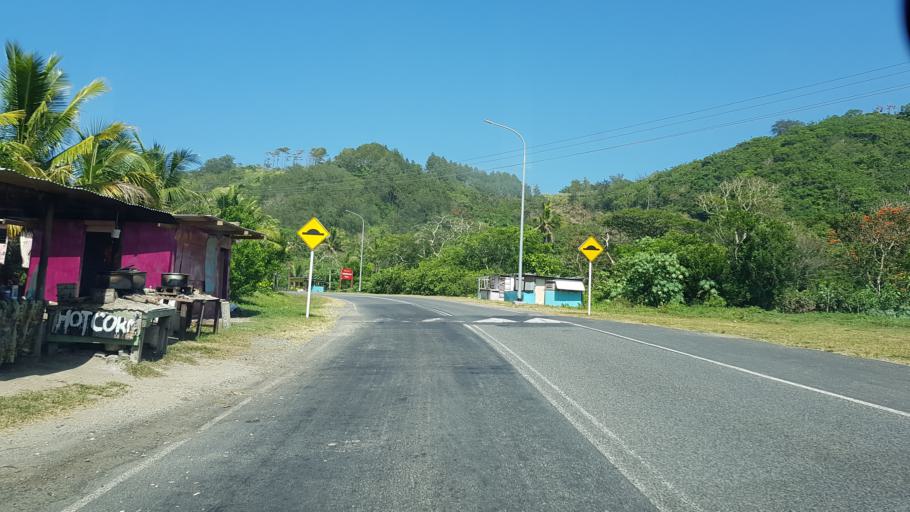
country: FJ
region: Western
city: Nadi
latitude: -18.1816
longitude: 177.6072
